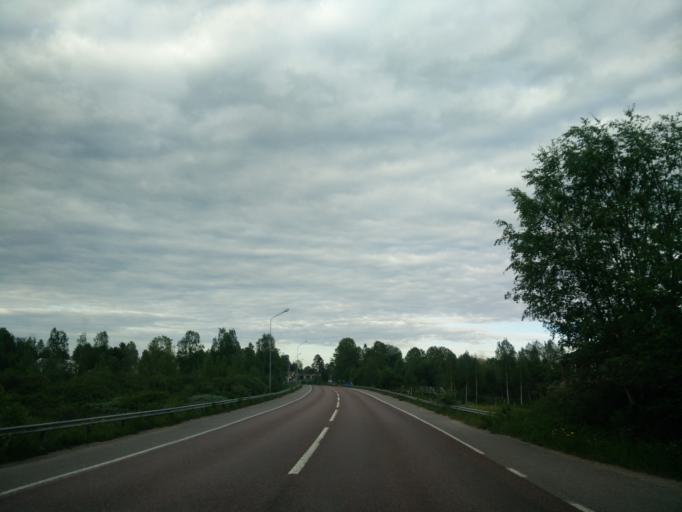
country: SE
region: Jaemtland
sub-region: Harjedalens Kommun
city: Sveg
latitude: 62.1738
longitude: 14.9328
